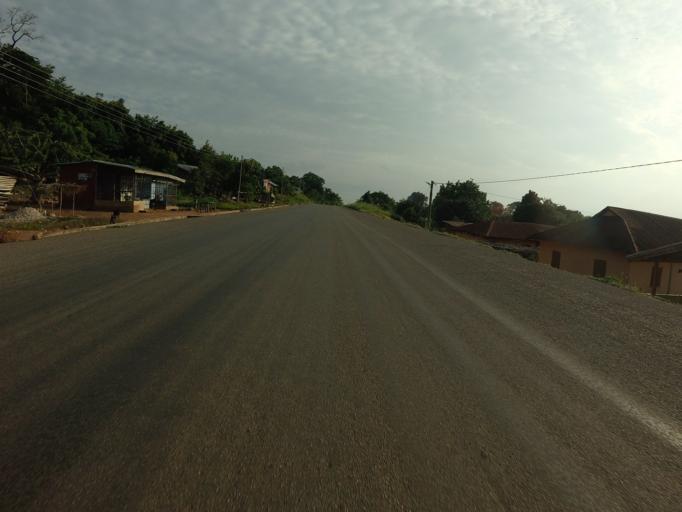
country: GH
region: Volta
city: Kpandu
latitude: 6.9125
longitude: 0.4493
